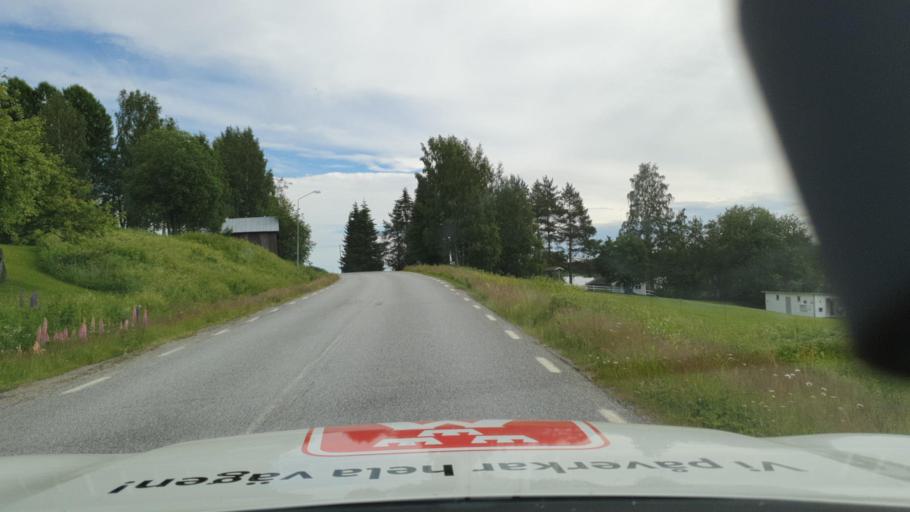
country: SE
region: Vaesterbotten
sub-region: Skelleftea Kommun
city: Burea
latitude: 64.4951
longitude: 21.0209
